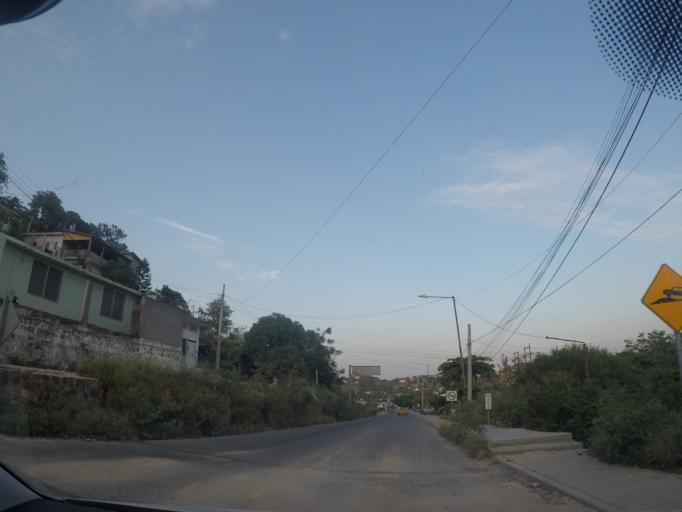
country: MX
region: Oaxaca
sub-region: Salina Cruz
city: Salina Cruz
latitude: 16.1931
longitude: -95.2090
